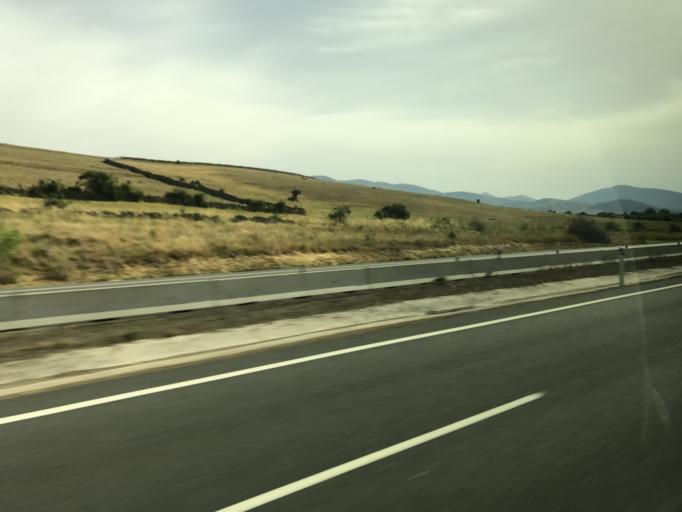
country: ES
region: Castille and Leon
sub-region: Provincia de Segovia
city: Vegas de Matute
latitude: 40.7397
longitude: -4.2425
